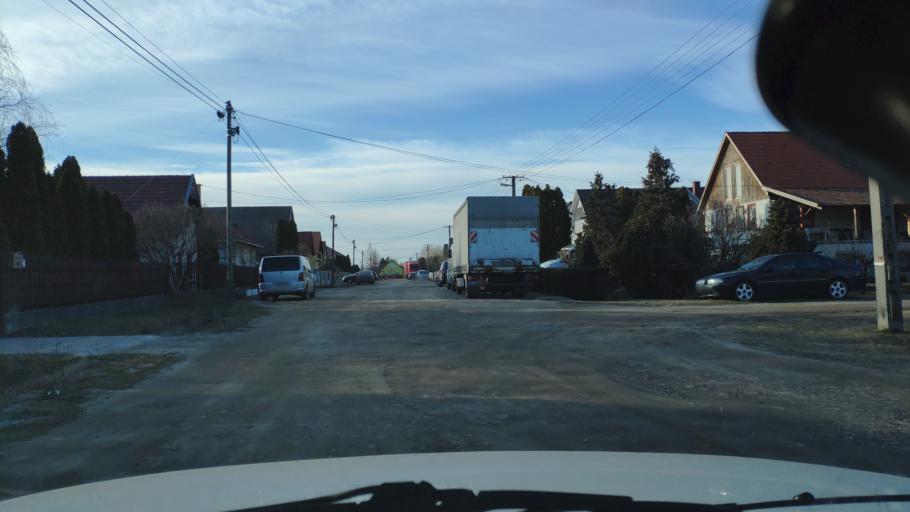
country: HU
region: Pest
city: Nyaregyhaza
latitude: 47.2631
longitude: 19.5084
